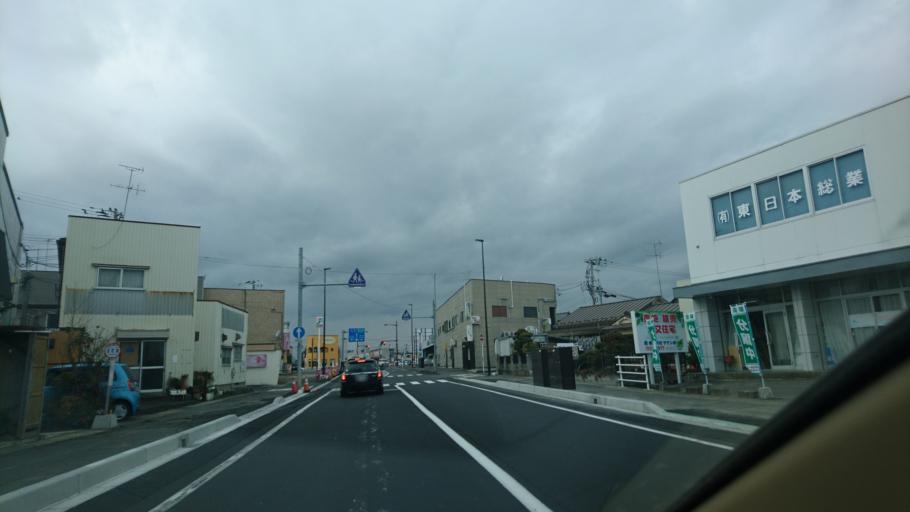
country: JP
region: Miyagi
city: Furukawa
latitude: 38.5773
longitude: 140.9630
